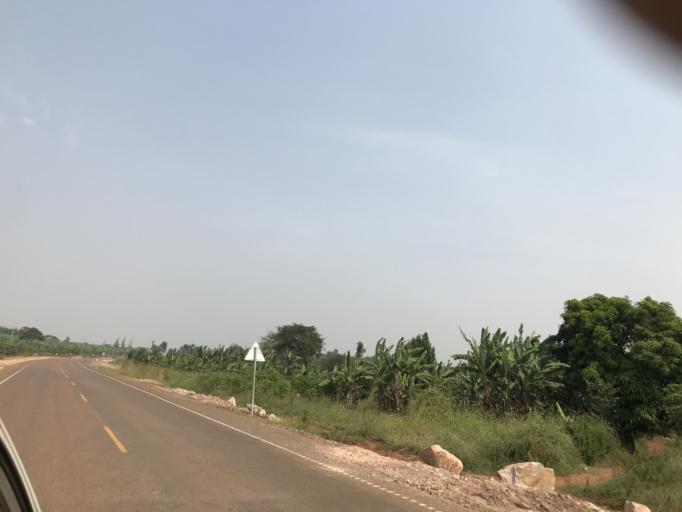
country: UG
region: Central Region
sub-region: Kalungu District
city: Kalungu
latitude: -0.2277
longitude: 31.7282
